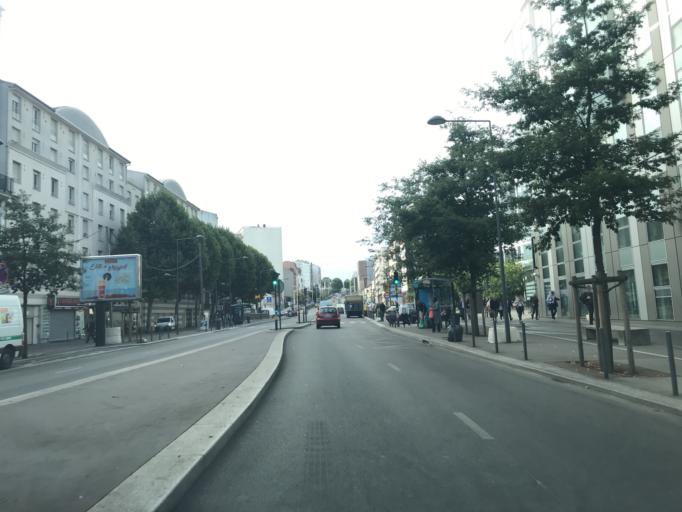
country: FR
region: Ile-de-France
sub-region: Departement du Val-de-Marne
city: Le Kremlin-Bicetre
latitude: 48.8055
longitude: 2.3636
